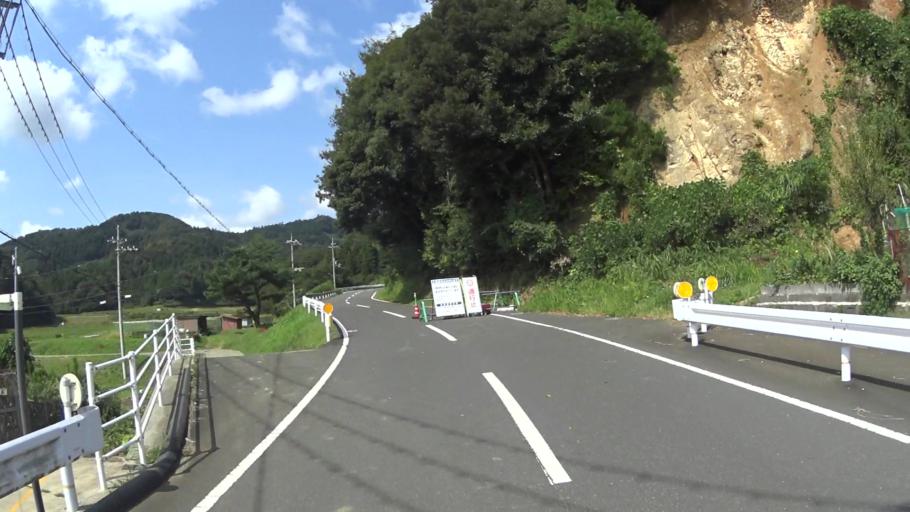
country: JP
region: Kyoto
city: Miyazu
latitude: 35.6747
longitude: 135.2718
